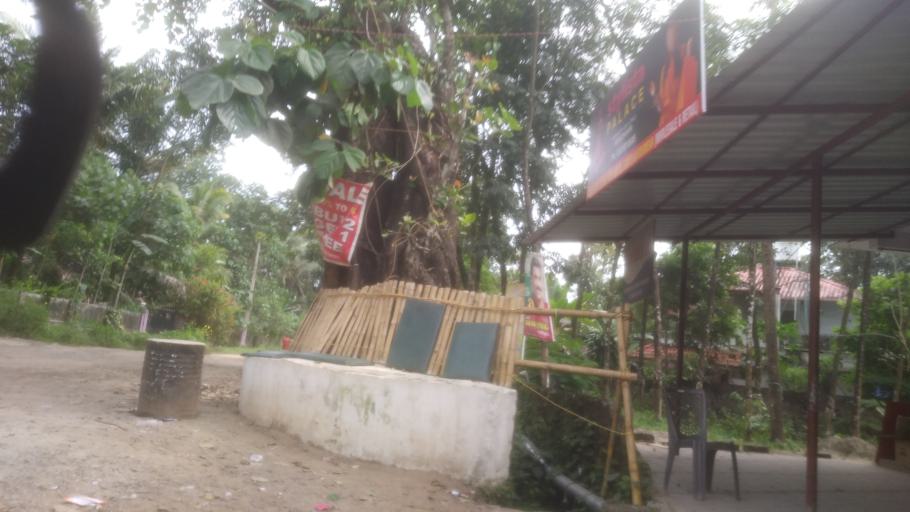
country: IN
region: Kerala
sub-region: Ernakulam
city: Perumbavoor
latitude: 10.0521
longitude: 76.5216
